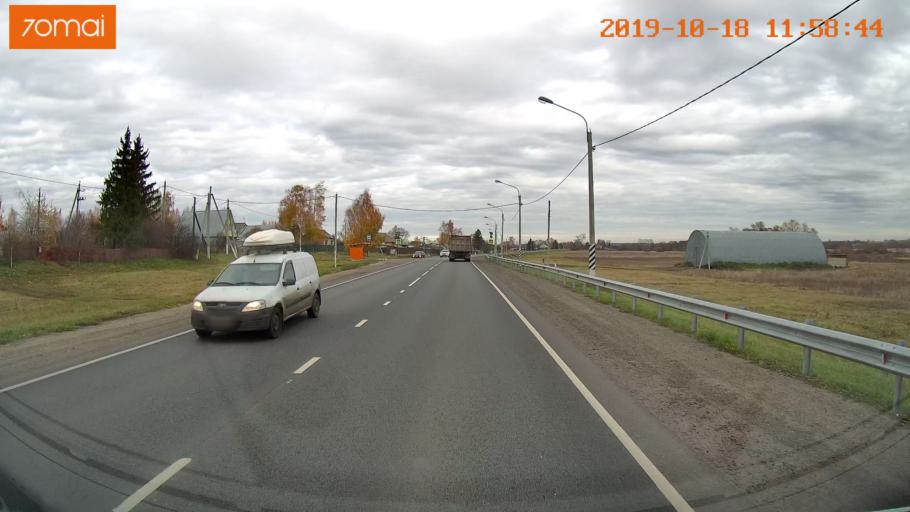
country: RU
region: Rjazan
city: Zakharovo
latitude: 54.2746
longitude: 39.1693
